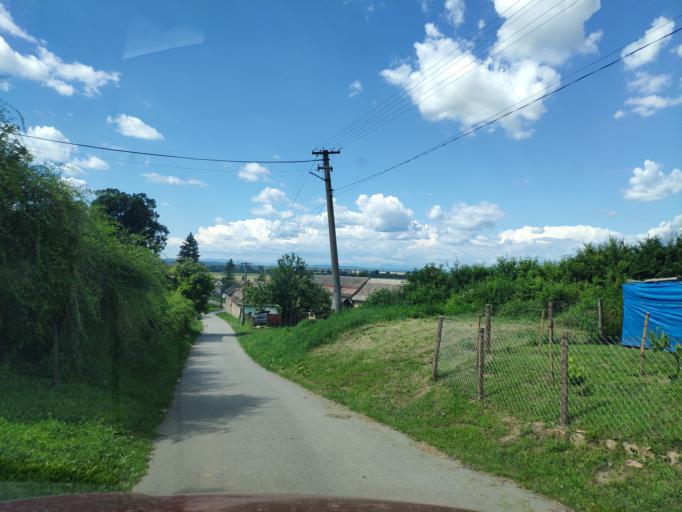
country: HU
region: Borsod-Abauj-Zemplen
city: Arlo
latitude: 48.2770
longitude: 20.1854
